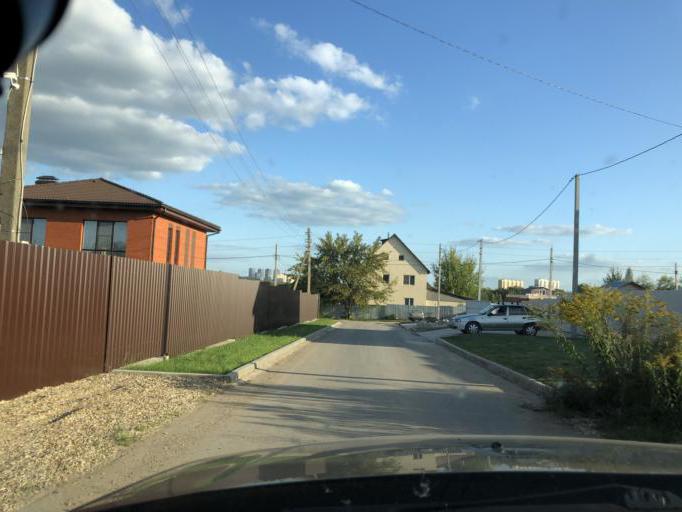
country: RU
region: Tula
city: Kosaya Gora
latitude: 54.1743
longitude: 37.5454
